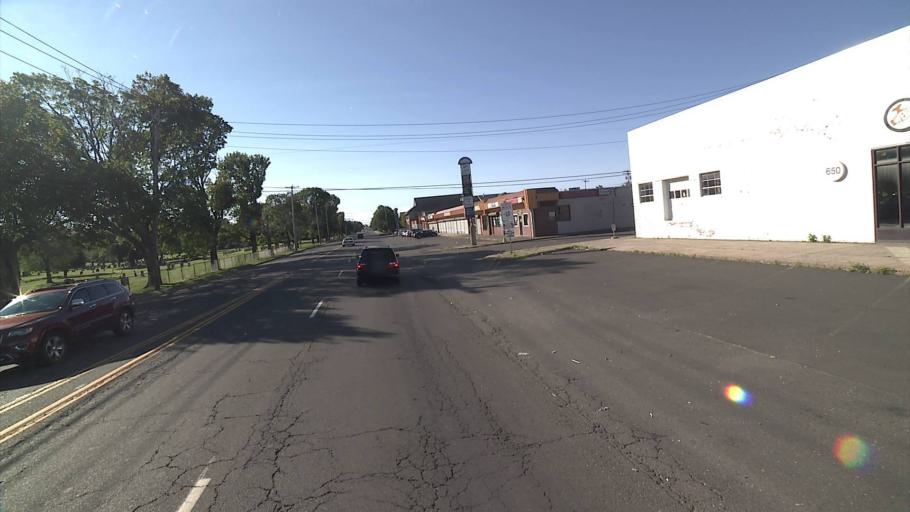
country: US
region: Connecticut
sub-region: New Haven County
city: New Haven
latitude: 41.2963
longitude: -72.9478
